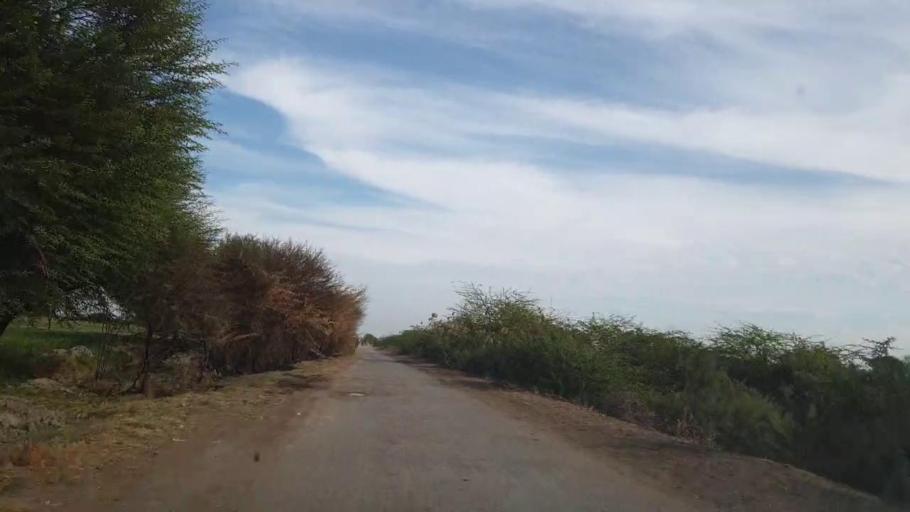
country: PK
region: Sindh
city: Pithoro
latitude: 25.6307
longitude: 69.4065
